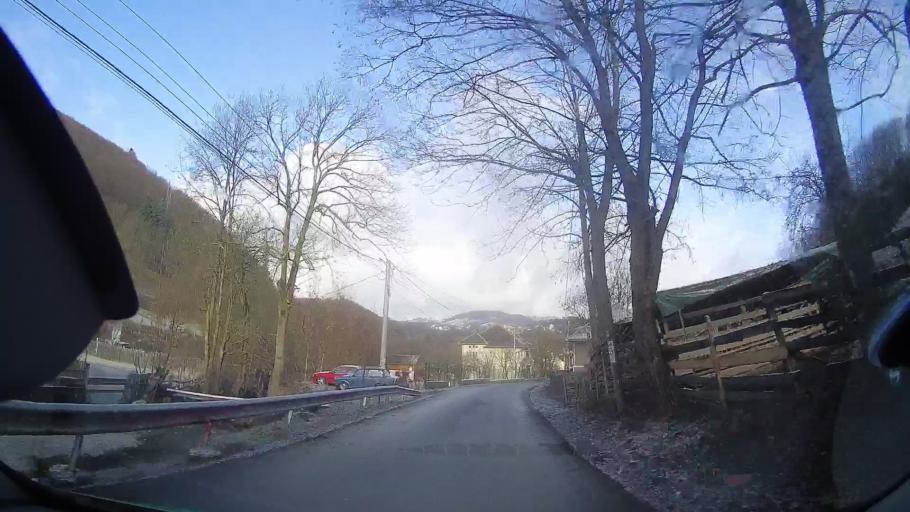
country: RO
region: Alba
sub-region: Comuna Sohodol
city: Sohodol
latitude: 46.3527
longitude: 23.0292
